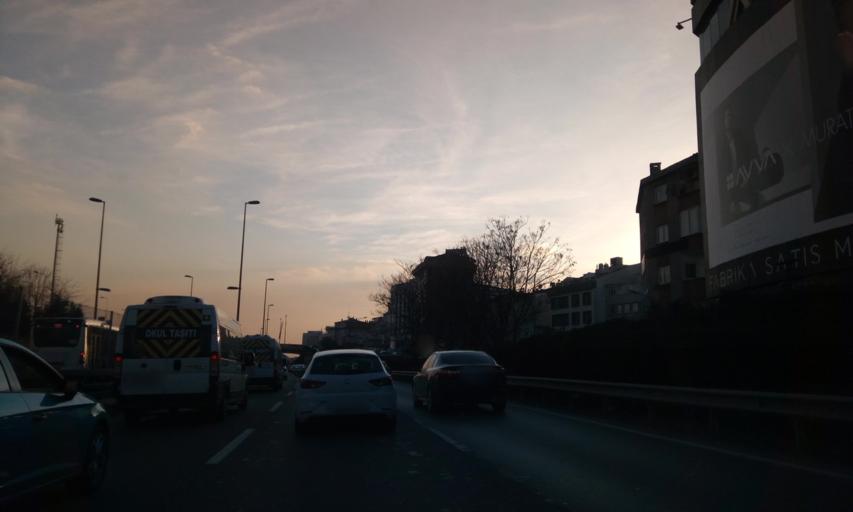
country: TR
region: Istanbul
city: Sisli
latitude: 41.0652
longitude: 28.9700
